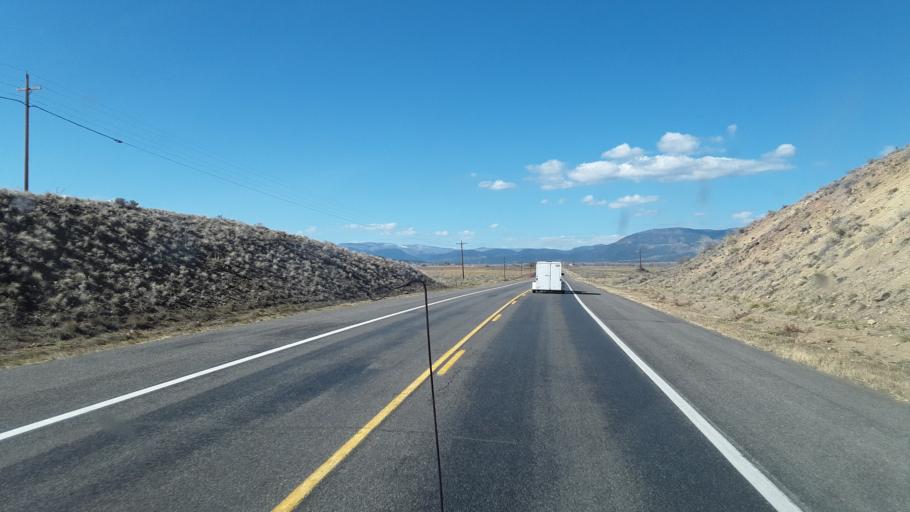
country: US
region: Colorado
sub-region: Rio Grande County
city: Del Norte
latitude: 37.6734
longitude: -106.4144
